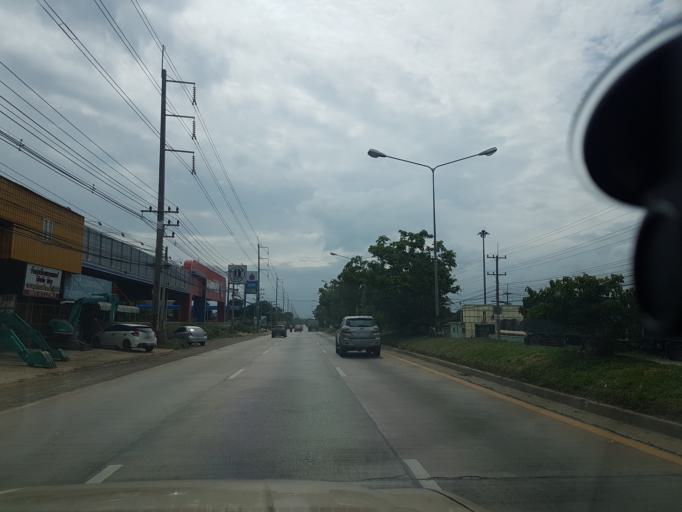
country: TH
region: Sara Buri
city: Phra Phutthabat
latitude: 14.7114
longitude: 100.8287
